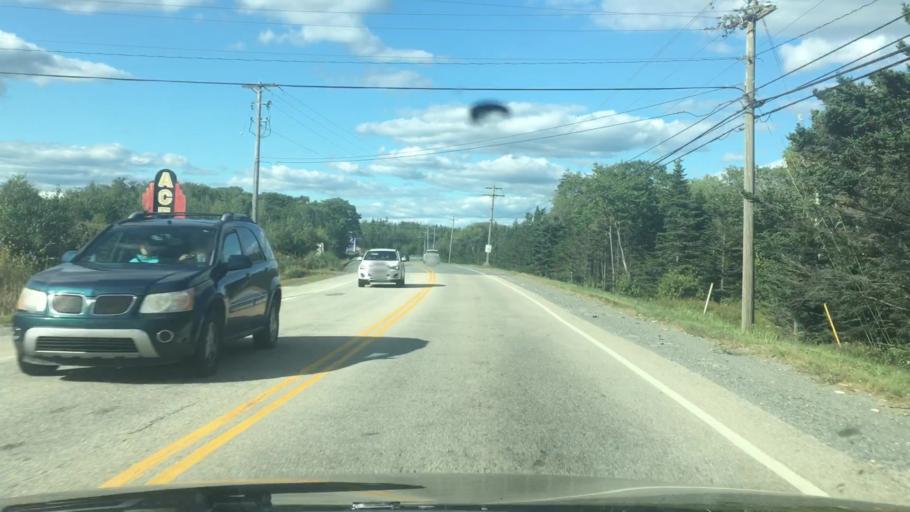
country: CA
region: Nova Scotia
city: Halifax
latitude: 44.6049
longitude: -63.6730
